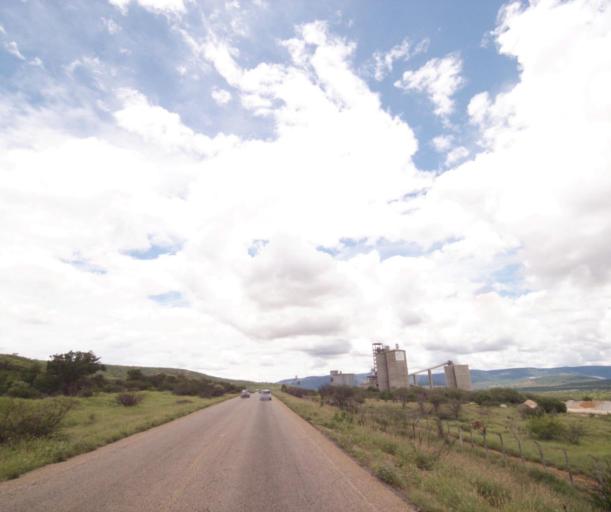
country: BR
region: Bahia
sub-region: Brumado
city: Brumado
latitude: -14.1984
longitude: -41.5941
